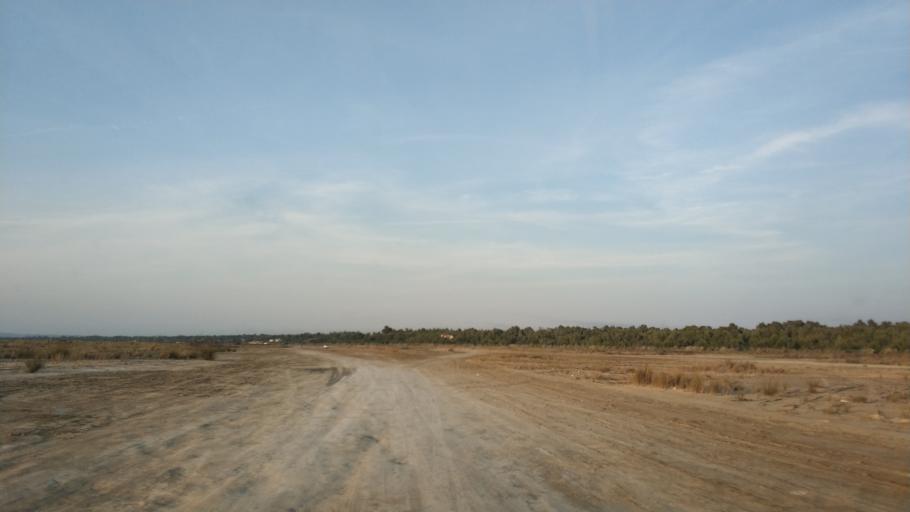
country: AL
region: Fier
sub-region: Rrethi i Lushnjes
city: Divjake
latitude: 40.9579
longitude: 19.4700
